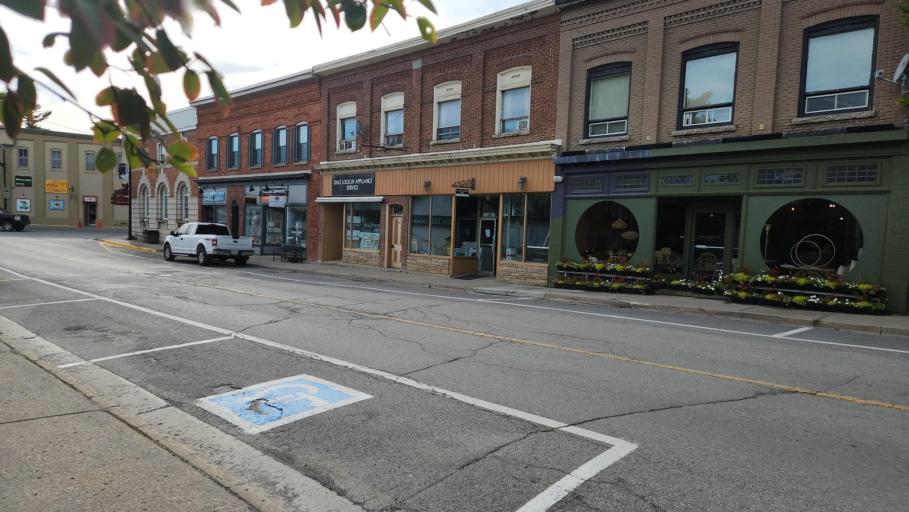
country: CA
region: Ontario
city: Quinte West
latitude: 44.2967
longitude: -77.5470
